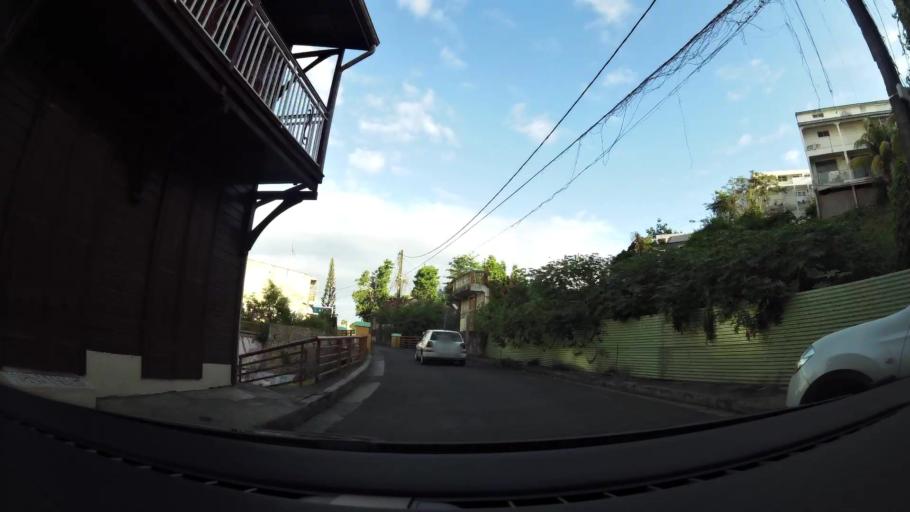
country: GP
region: Guadeloupe
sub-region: Guadeloupe
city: Pointe-a-Pitre
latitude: 16.2351
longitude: -61.5328
